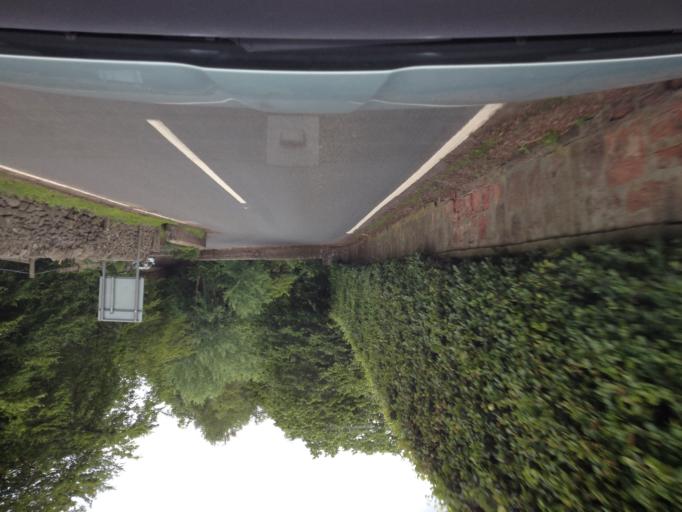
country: GB
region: Scotland
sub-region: Angus
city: Brechin
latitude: 56.8273
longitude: -2.6572
